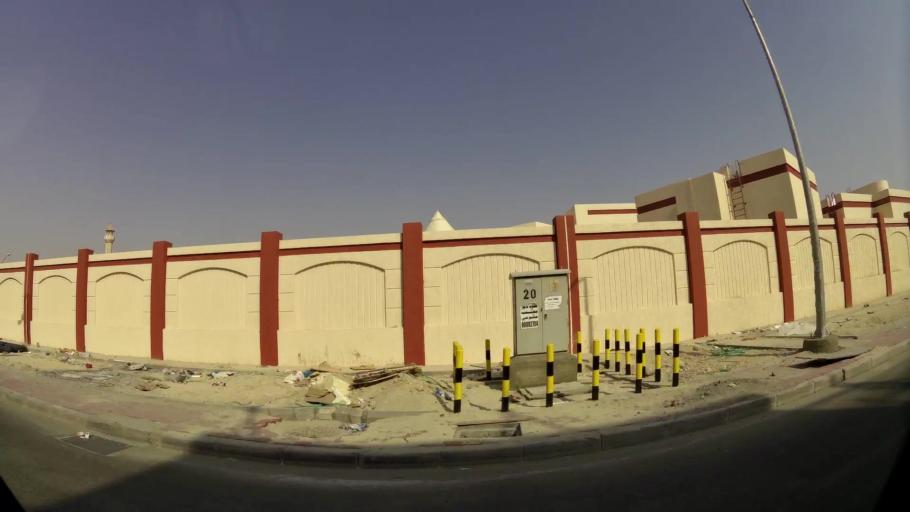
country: KW
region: Muhafazat al Jahra'
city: Al Jahra'
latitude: 29.3503
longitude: 47.7642
